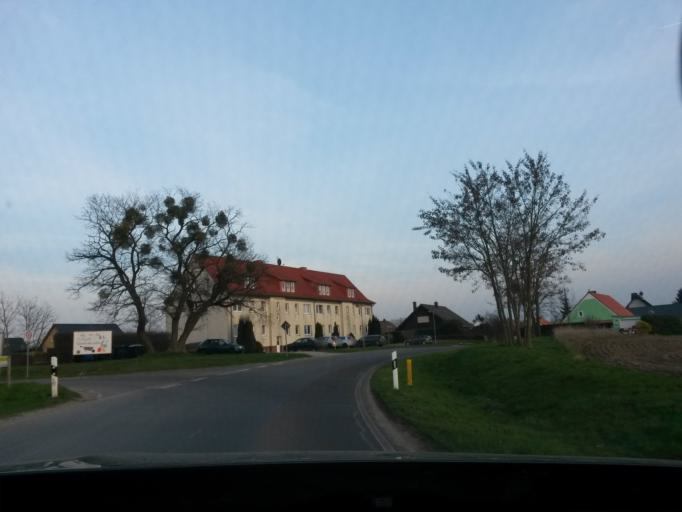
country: DE
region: Brandenburg
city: Protzel
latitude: 52.5942
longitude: 13.9476
